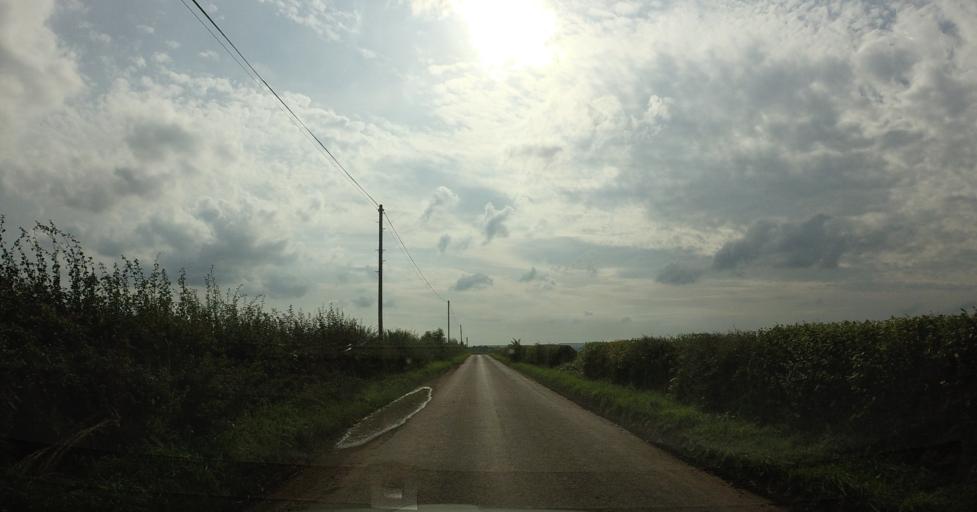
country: GB
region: Scotland
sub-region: Perth and Kinross
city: Auchterarder
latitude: 56.3575
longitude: -3.7091
